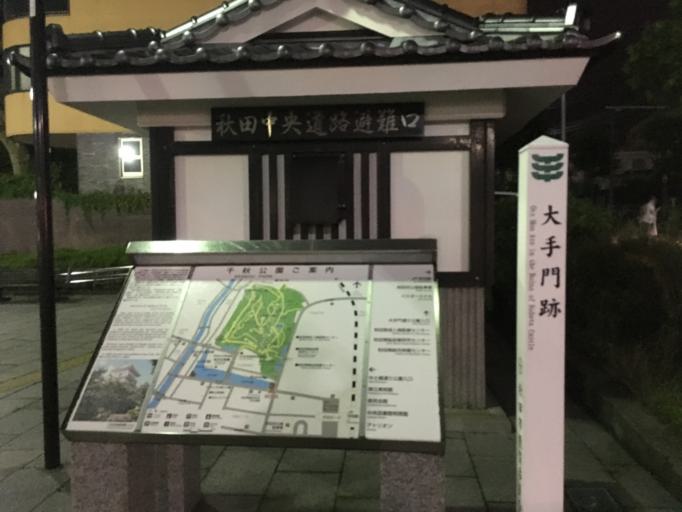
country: JP
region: Akita
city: Akita
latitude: 39.7178
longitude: 140.1254
